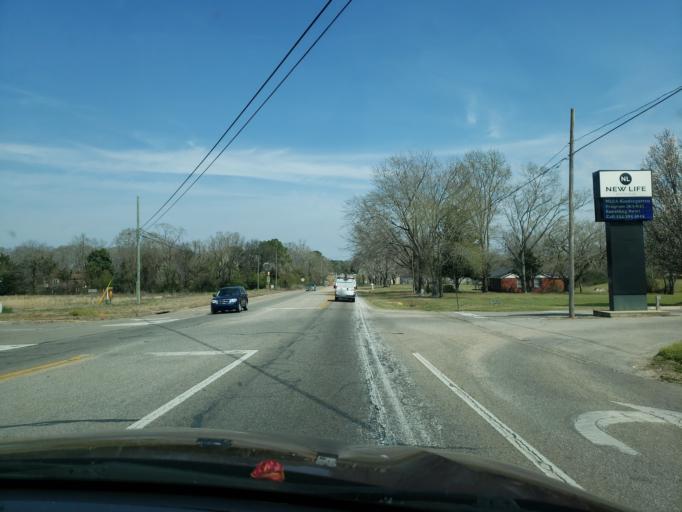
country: US
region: Alabama
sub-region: Elmore County
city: Millbrook
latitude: 32.5206
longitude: -86.3674
